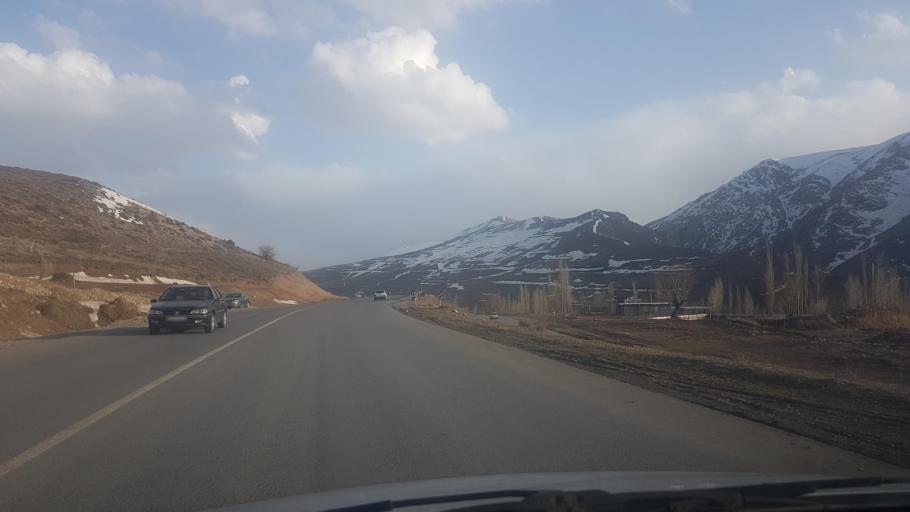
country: IR
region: Ardabil
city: Khalkhal
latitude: 37.5753
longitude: 48.5937
